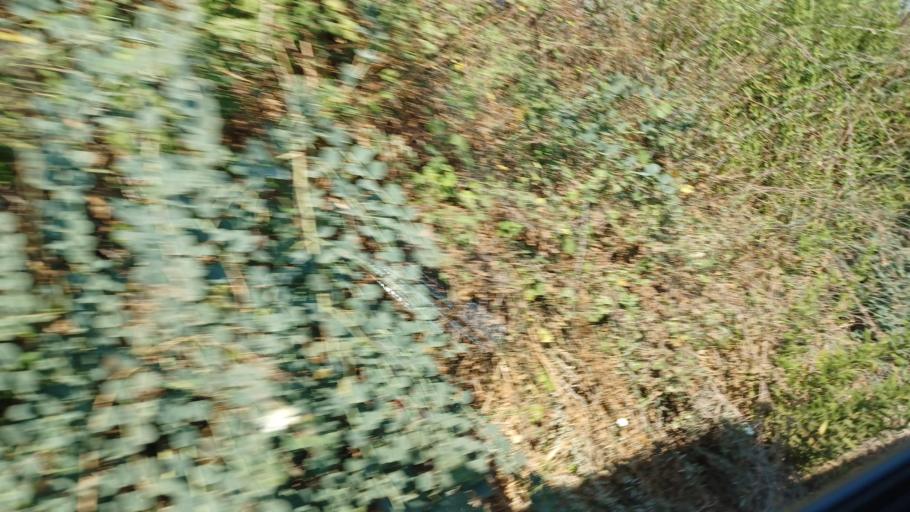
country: CY
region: Pafos
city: Tala
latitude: 34.8969
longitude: 32.5017
